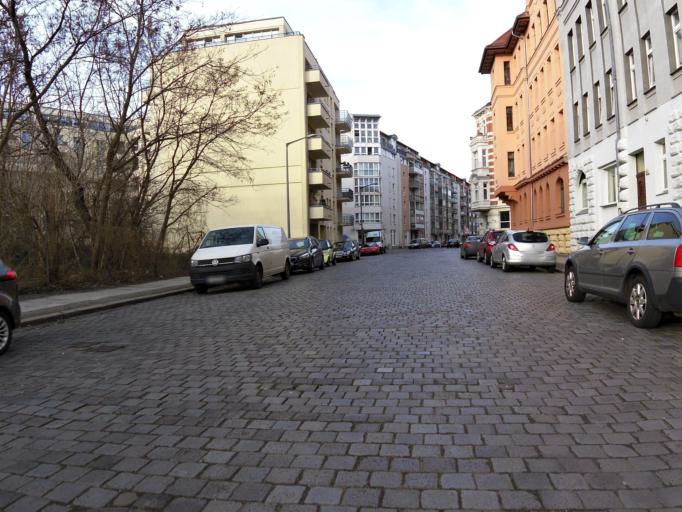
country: DE
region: Saxony
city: Leipzig
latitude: 51.3433
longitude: 12.3968
